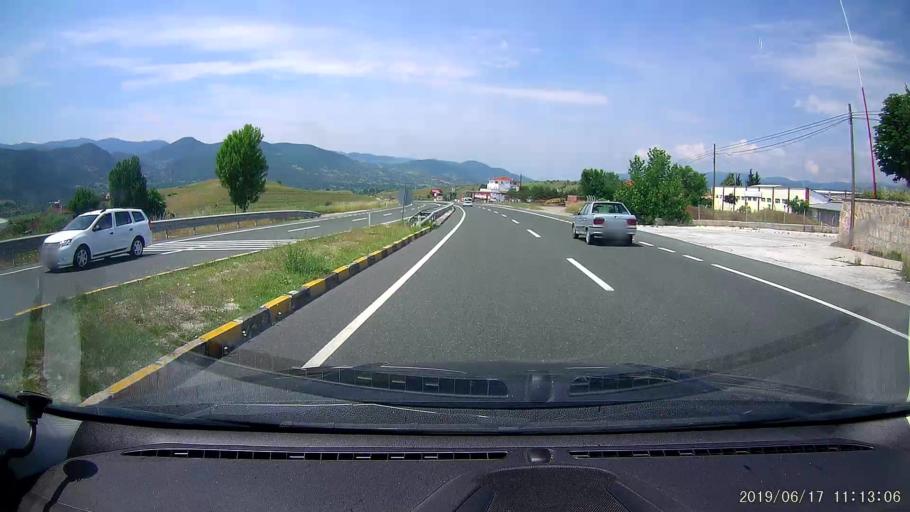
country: TR
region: Kastamonu
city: Tosya
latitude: 40.9669
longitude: 33.9793
